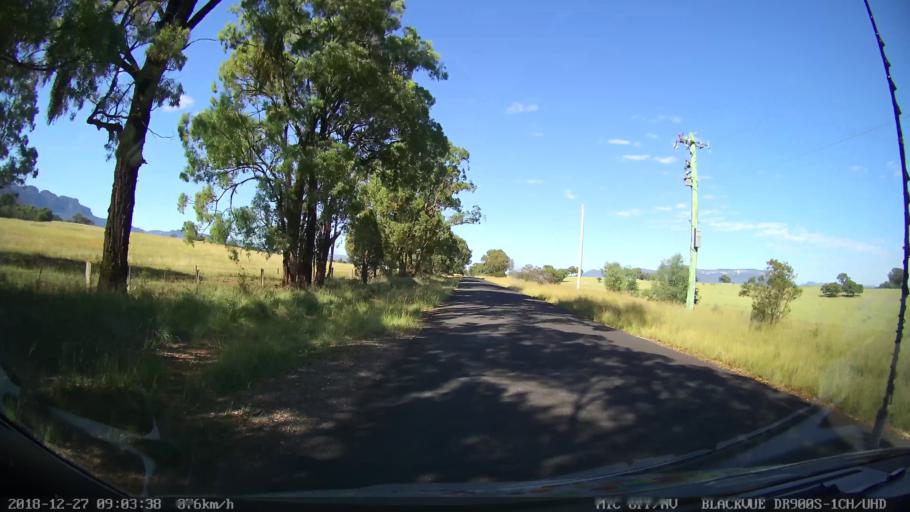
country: AU
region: New South Wales
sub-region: Lithgow
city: Portland
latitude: -33.1059
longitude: 150.1996
